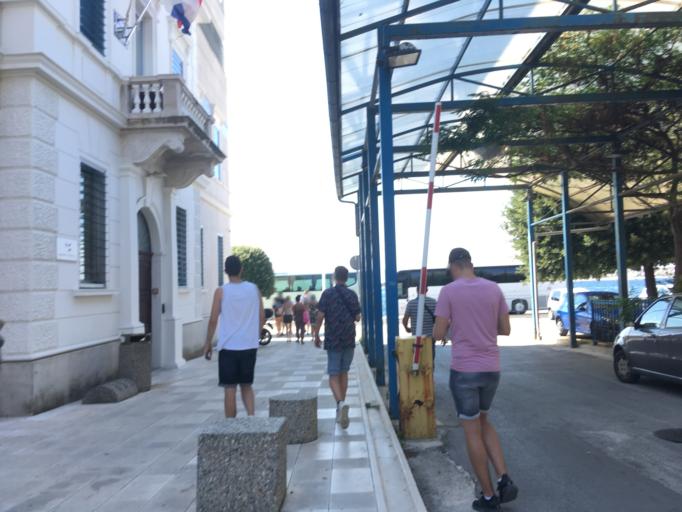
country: HR
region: Zadarska
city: Zadar
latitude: 44.1180
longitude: 15.2217
